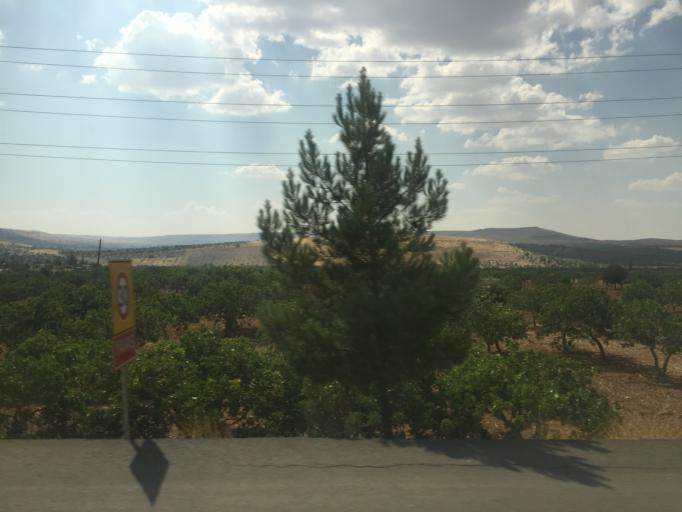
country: TR
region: Sanliurfa
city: Sanliurfa
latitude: 37.2414
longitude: 38.7938
